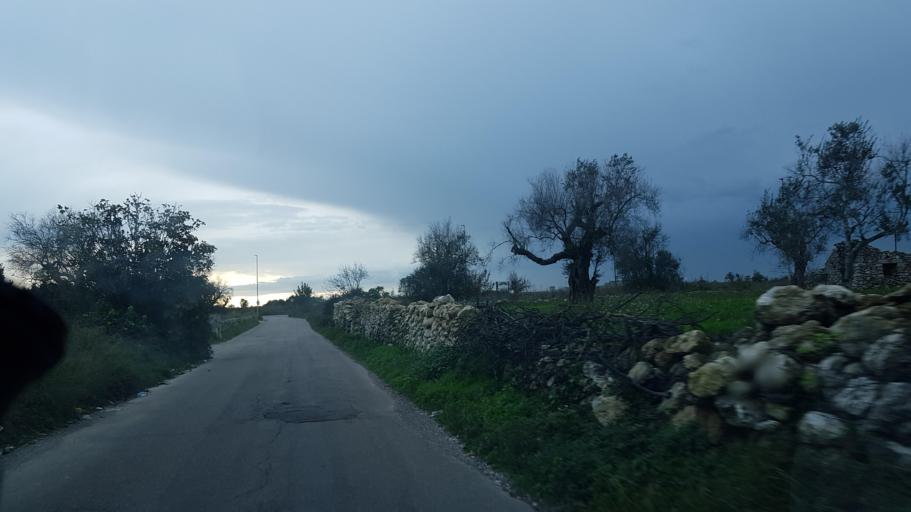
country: IT
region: Apulia
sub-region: Provincia di Lecce
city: Merine
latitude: 40.3256
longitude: 18.2243
